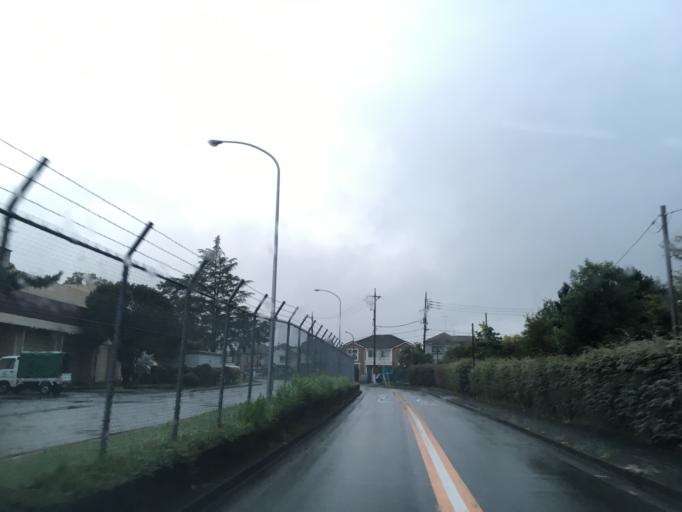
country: JP
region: Tokyo
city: Fussa
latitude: 35.7378
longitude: 139.3630
